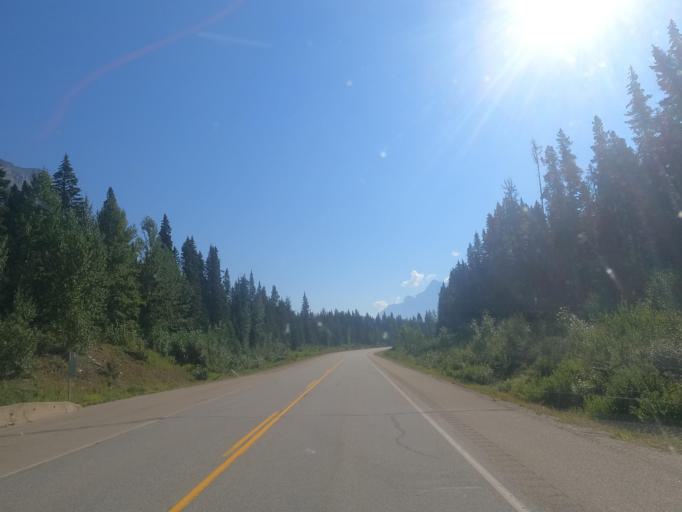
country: CA
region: Alberta
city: Jasper Park Lodge
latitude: 52.8627
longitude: -118.6476
